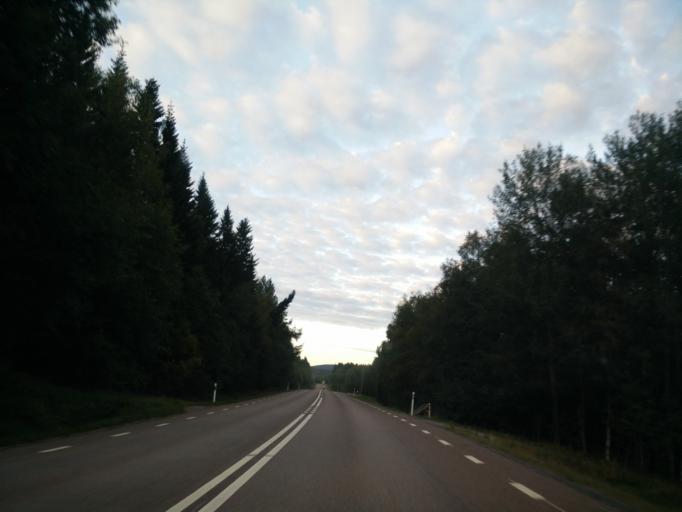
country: SE
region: Vaesternorrland
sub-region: Kramfors Kommun
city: Nordingra
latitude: 62.9201
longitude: 18.0657
